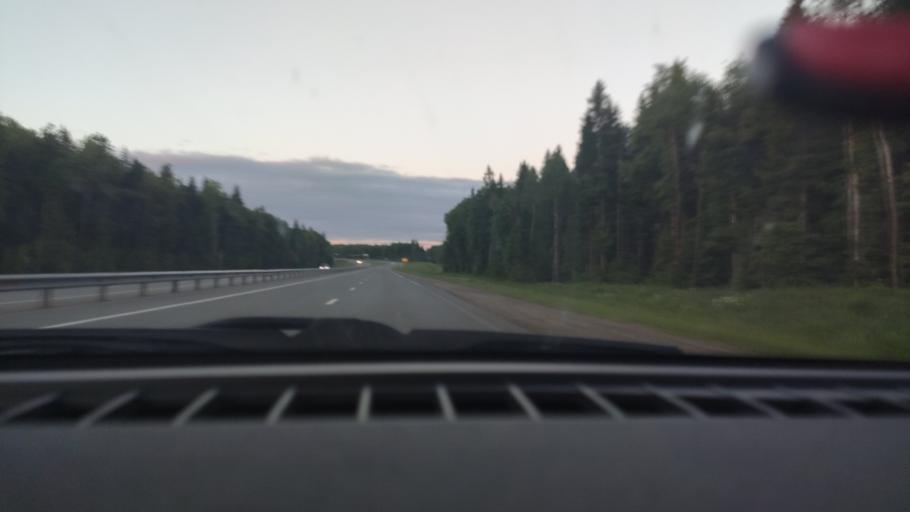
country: RU
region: Perm
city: Polazna
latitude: 58.2590
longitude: 56.4105
